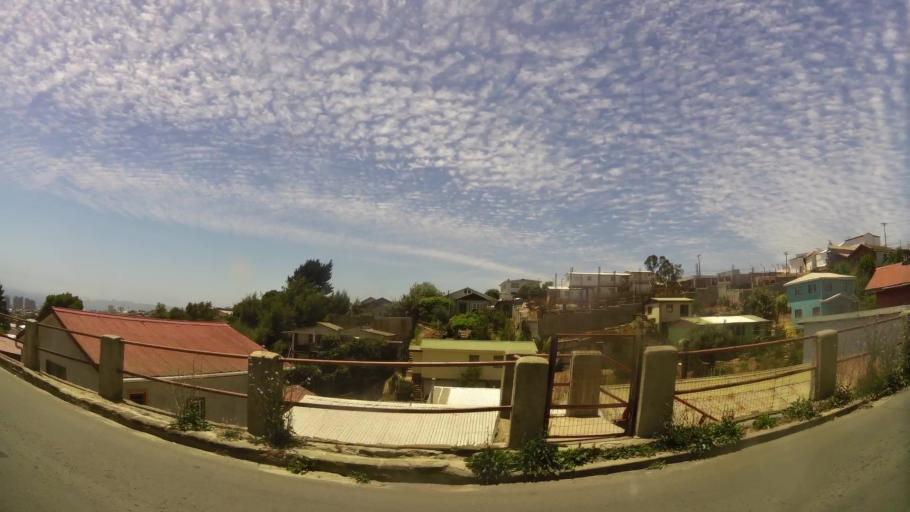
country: CL
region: Valparaiso
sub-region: Provincia de Valparaiso
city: Vina del Mar
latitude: -33.0449
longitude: -71.5869
